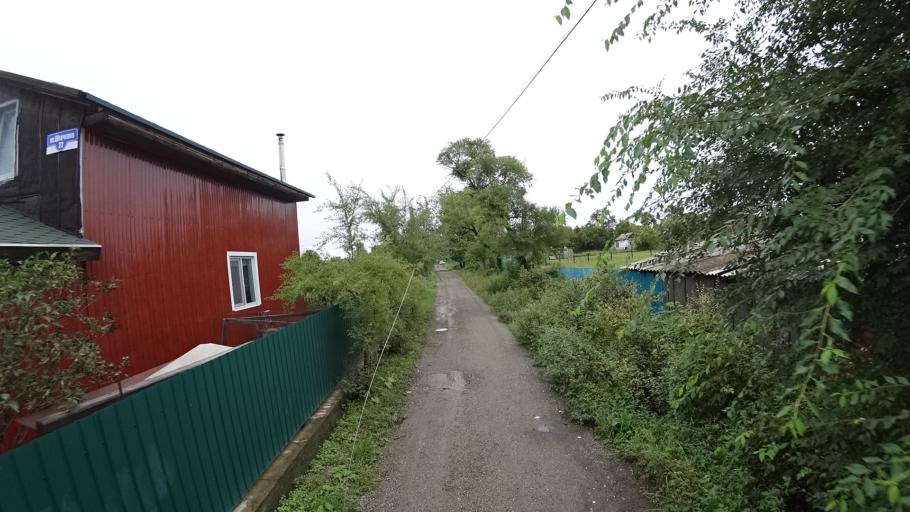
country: RU
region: Primorskiy
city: Monastyrishche
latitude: 44.2076
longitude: 132.4321
